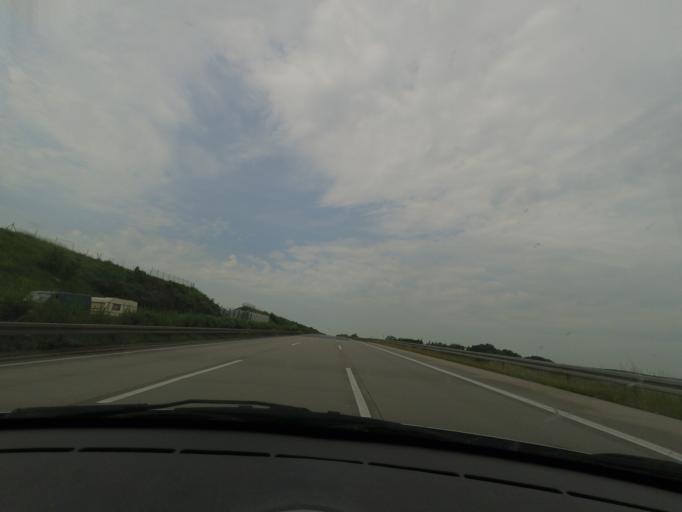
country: DE
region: Thuringia
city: Hartmannsdorf
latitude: 50.9051
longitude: 12.0138
